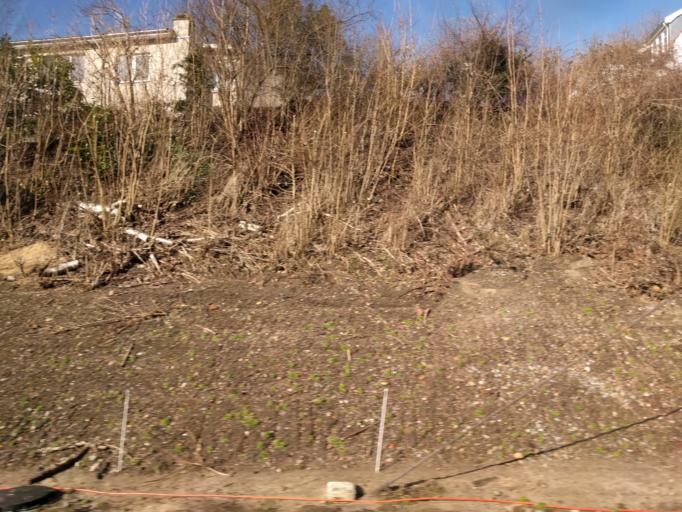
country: DK
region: Capital Region
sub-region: Helsingor Kommune
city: Helsingor
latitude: 56.0218
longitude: 12.6016
